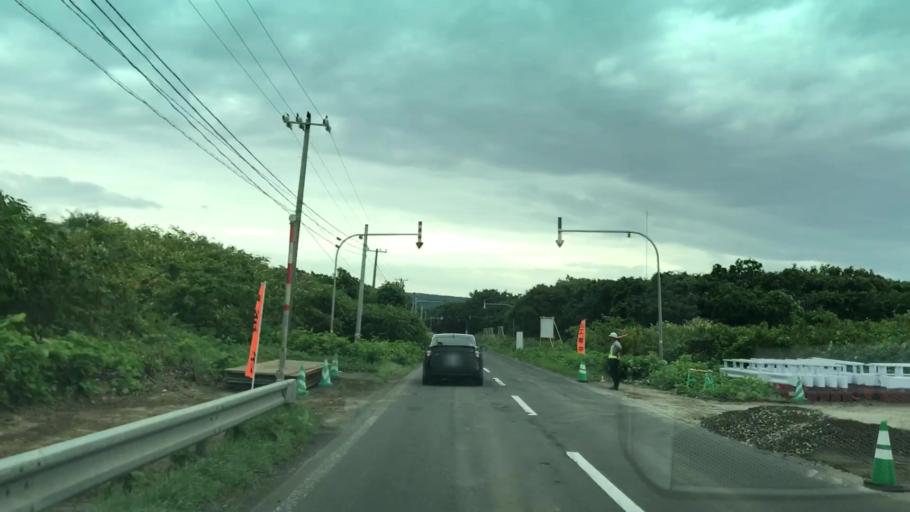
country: JP
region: Hokkaido
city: Iwanai
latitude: 42.8907
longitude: 140.3750
